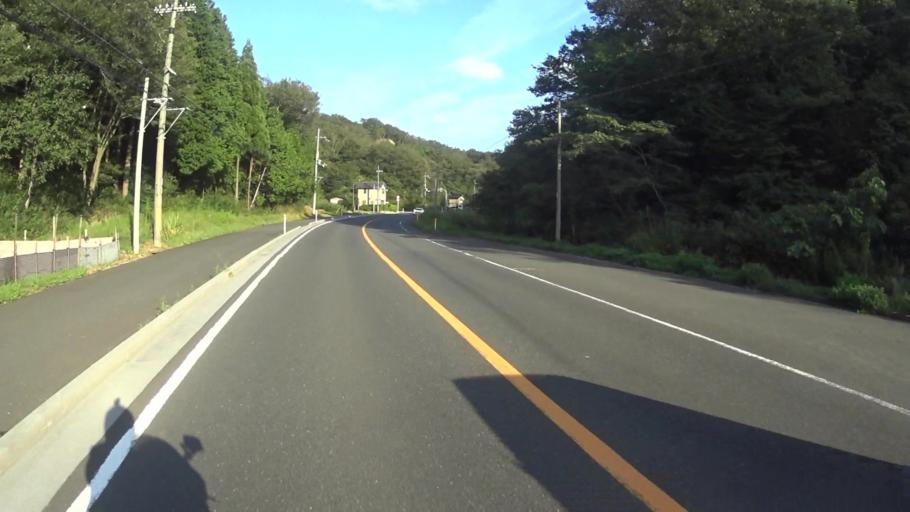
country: JP
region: Hyogo
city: Toyooka
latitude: 35.5865
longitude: 134.9502
